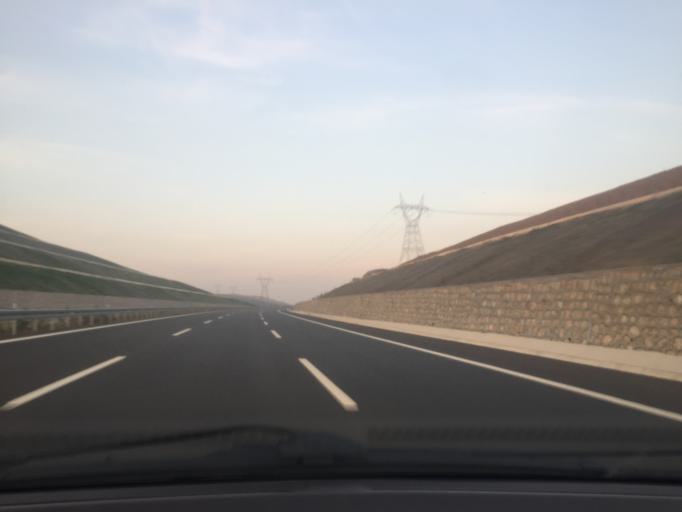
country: TR
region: Bursa
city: Mahmudiye
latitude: 40.2742
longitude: 28.5568
